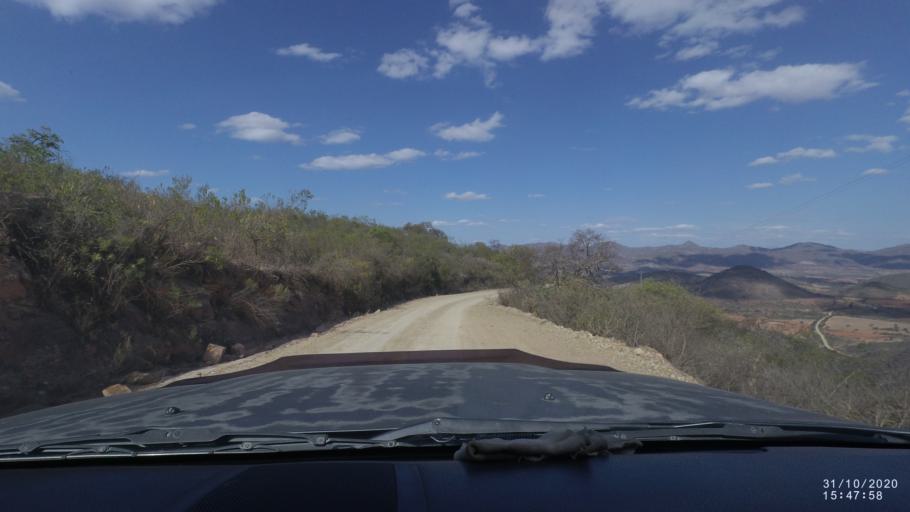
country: BO
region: Chuquisaca
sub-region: Provincia Zudanez
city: Mojocoya
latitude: -18.3137
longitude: -64.7129
